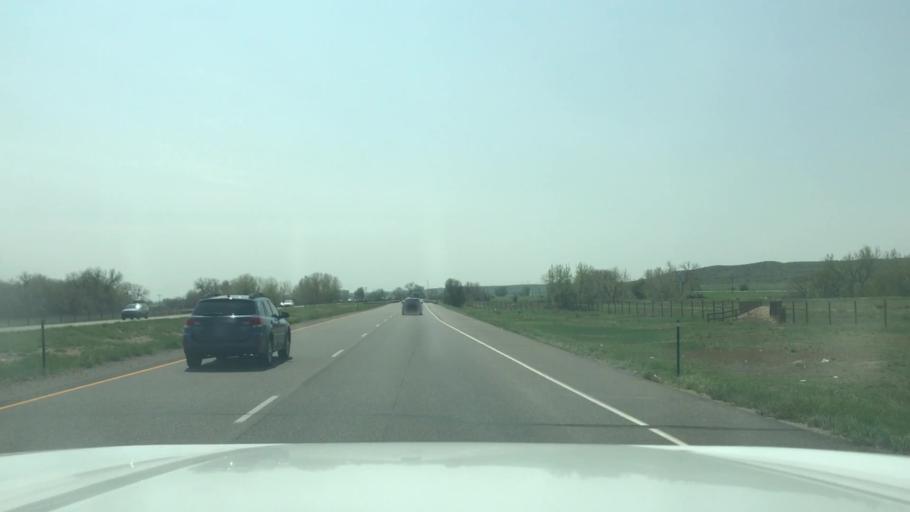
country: US
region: Colorado
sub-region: El Paso County
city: Fountain
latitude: 38.6242
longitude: -104.6899
